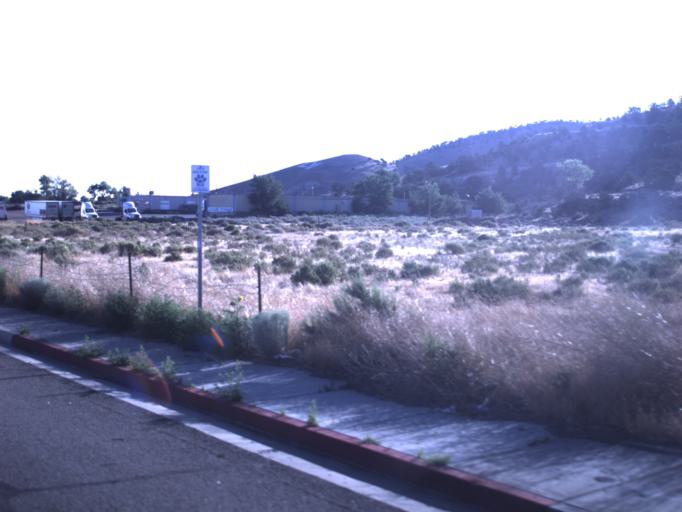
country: US
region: Utah
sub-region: Iron County
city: Cedar City
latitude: 37.7012
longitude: -113.0638
